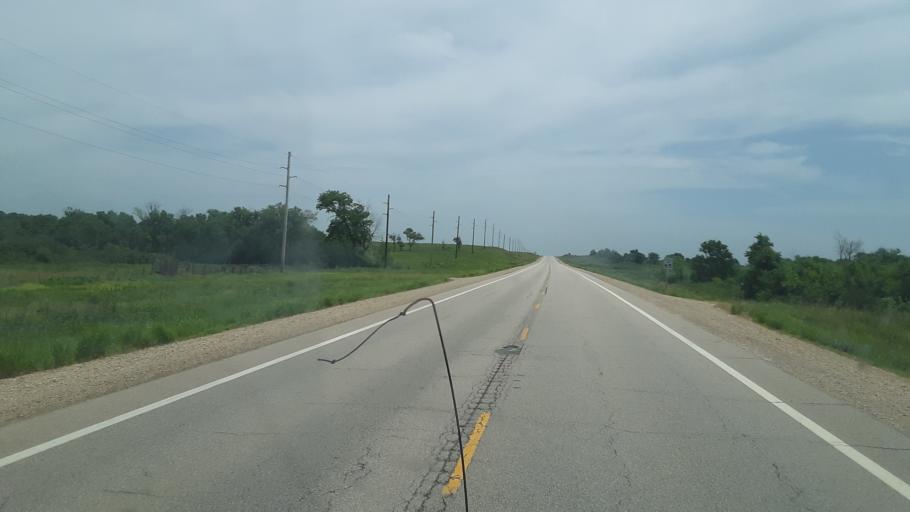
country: US
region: Kansas
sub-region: Greenwood County
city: Eureka
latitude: 37.8372
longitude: -96.0748
